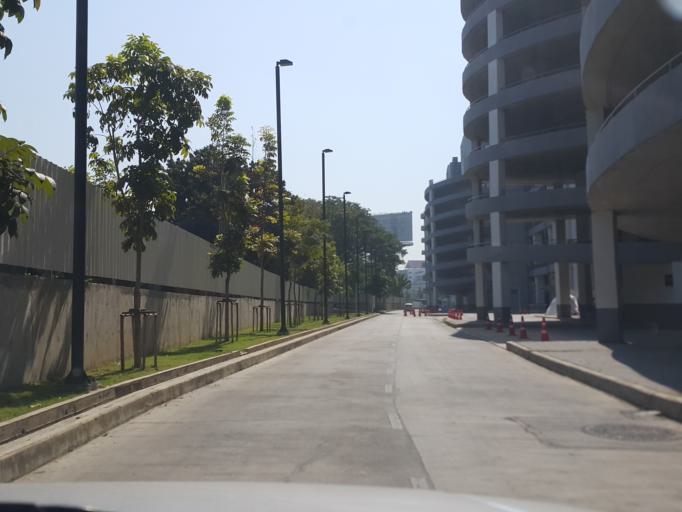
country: TH
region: Chiang Mai
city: Chiang Mai
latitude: 18.8086
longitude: 99.0190
